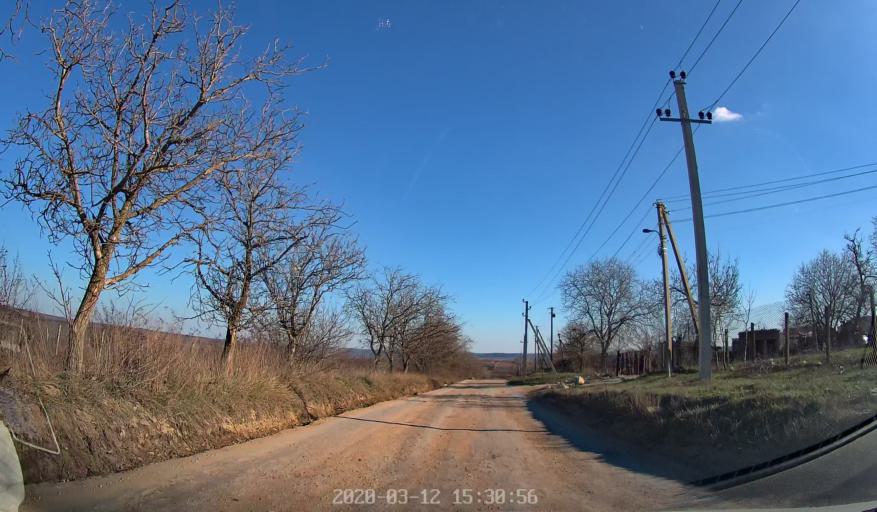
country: MD
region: Chisinau
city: Ciorescu
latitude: 47.1591
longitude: 28.9409
